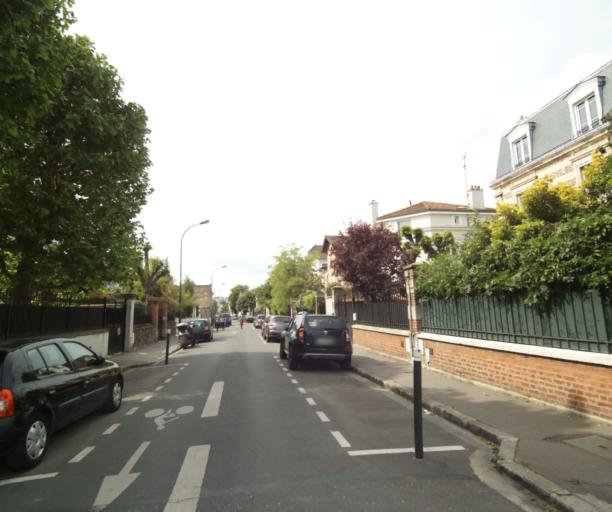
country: FR
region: Ile-de-France
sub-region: Departement des Hauts-de-Seine
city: Asnieres-sur-Seine
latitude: 48.9112
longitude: 2.2811
